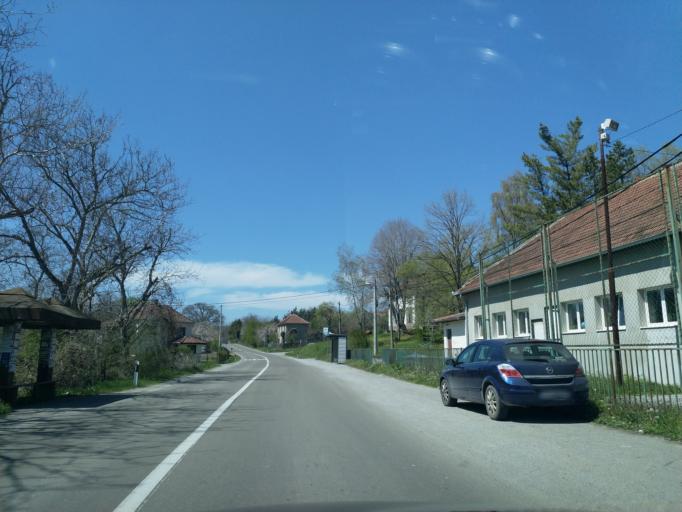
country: RS
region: Central Serbia
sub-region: Belgrade
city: Lazarevac
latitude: 44.3533
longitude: 20.3731
